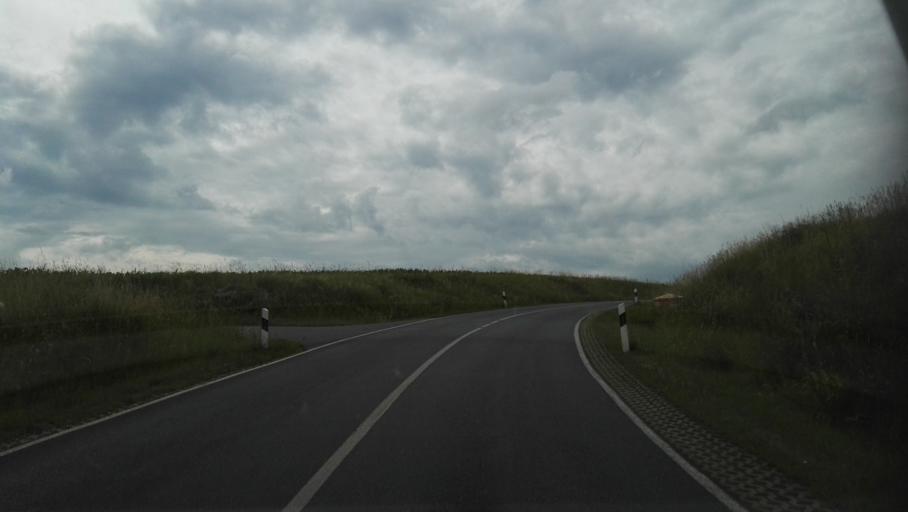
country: DE
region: Bavaria
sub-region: Upper Franconia
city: Plankenfels
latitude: 49.8818
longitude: 11.3364
